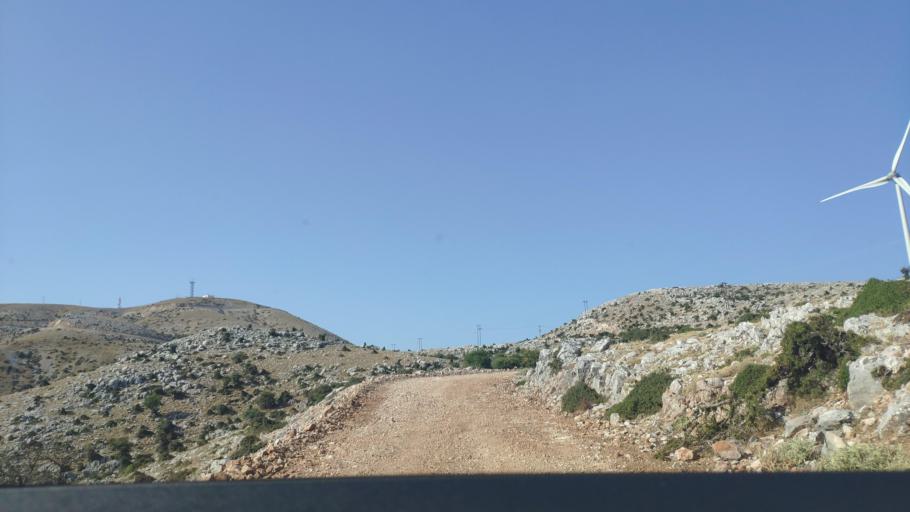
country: GR
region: West Greece
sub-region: Nomos Aitolias kai Akarnanias
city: Monastirakion
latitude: 38.8186
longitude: 20.9811
